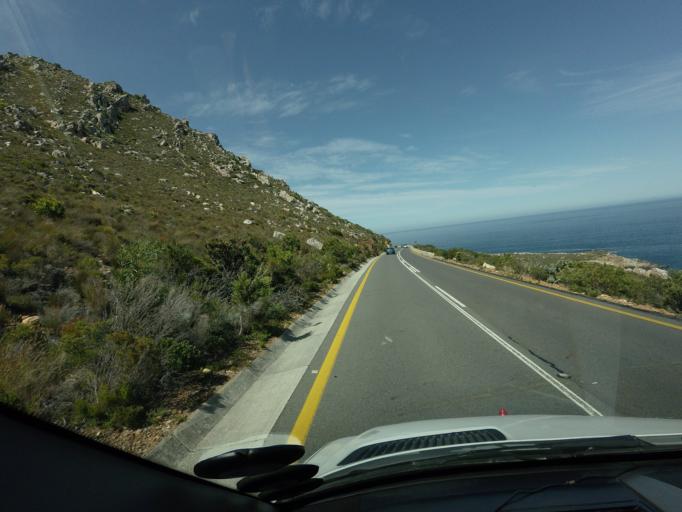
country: ZA
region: Western Cape
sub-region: Overberg District Municipality
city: Grabouw
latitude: -34.2145
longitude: 18.8351
